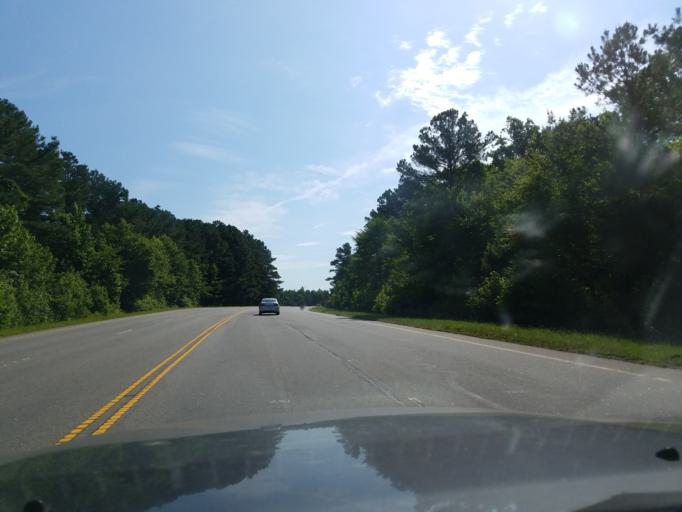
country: US
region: North Carolina
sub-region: Granville County
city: Oxford
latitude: 36.3146
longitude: -78.5503
